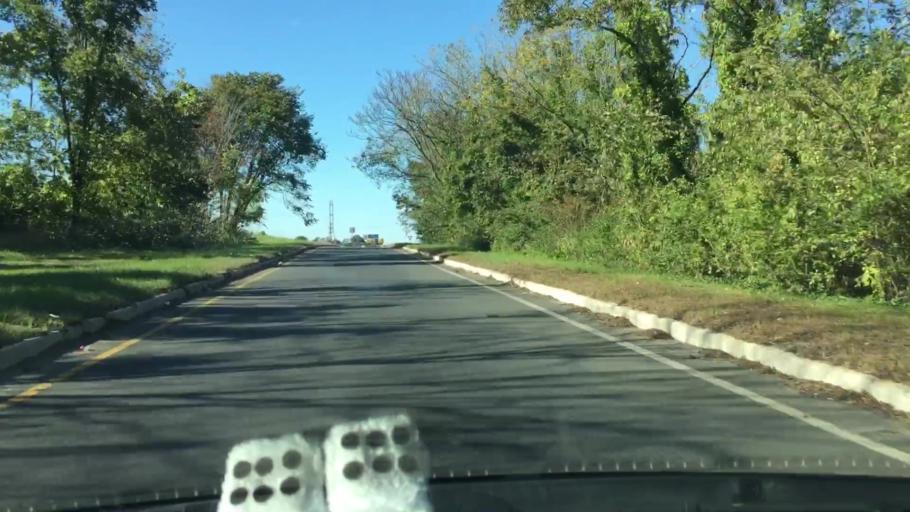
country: US
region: New Jersey
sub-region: Camden County
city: Blackwood
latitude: 39.8034
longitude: -75.0553
